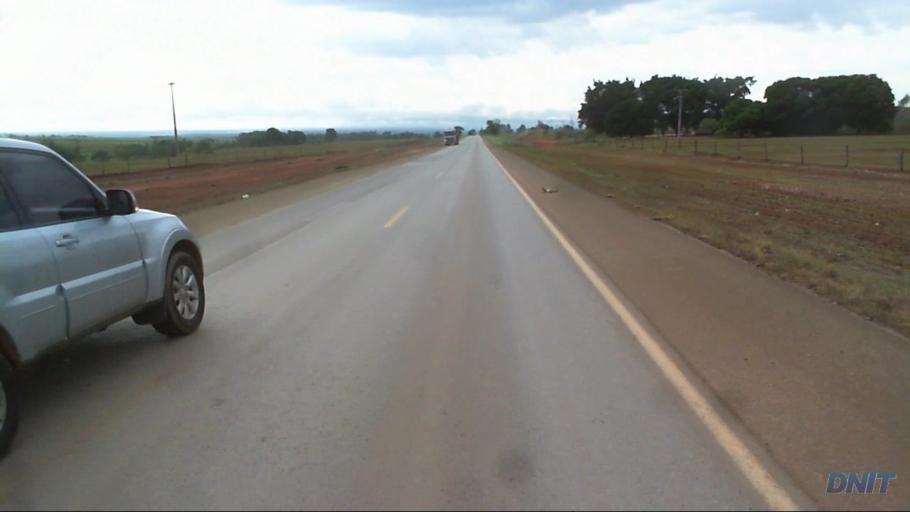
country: BR
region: Goias
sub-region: Uruacu
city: Uruacu
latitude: -14.7009
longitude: -49.1181
